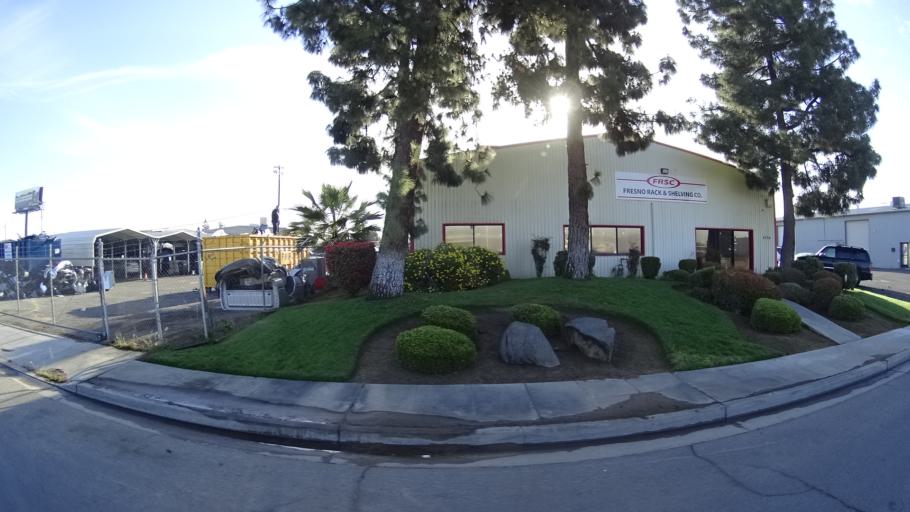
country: US
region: California
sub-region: Fresno County
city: West Park
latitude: 36.8069
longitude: -119.8700
